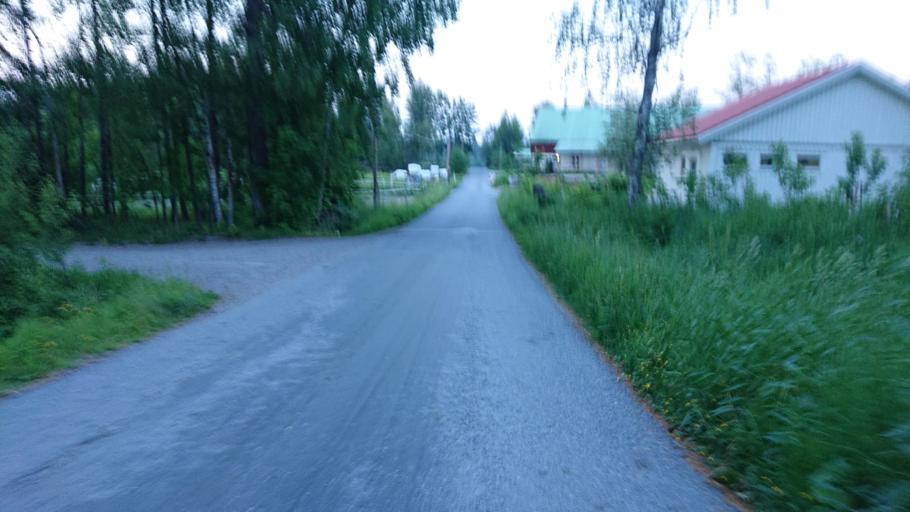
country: SE
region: Stockholm
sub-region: Osterakers Kommun
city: Akersberga
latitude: 59.4736
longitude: 18.2413
